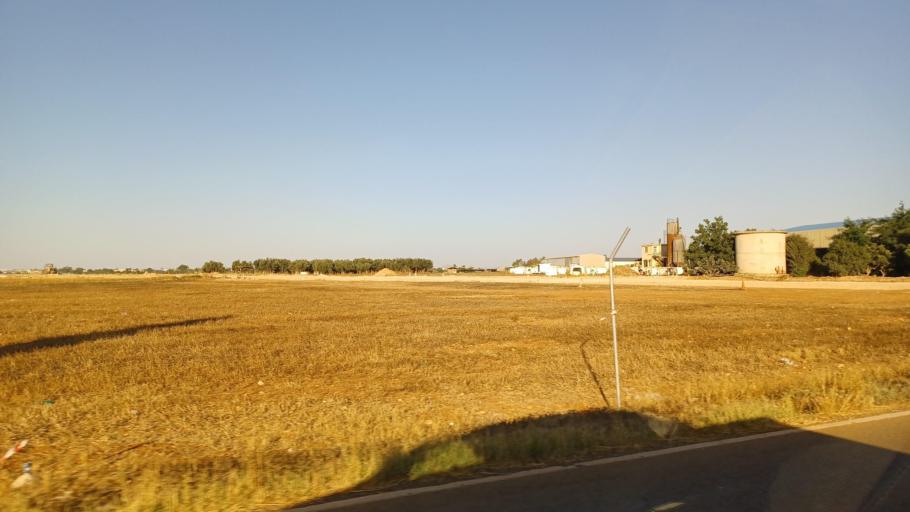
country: CY
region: Ammochostos
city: Achna
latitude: 35.0357
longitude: 33.7941
